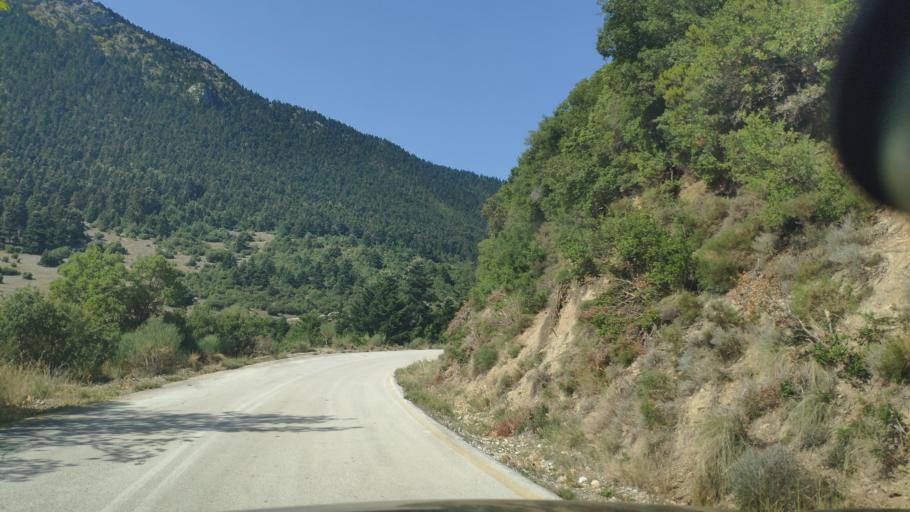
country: GR
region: Peloponnese
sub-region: Nomos Korinthias
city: Nemea
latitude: 37.8581
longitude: 22.3847
